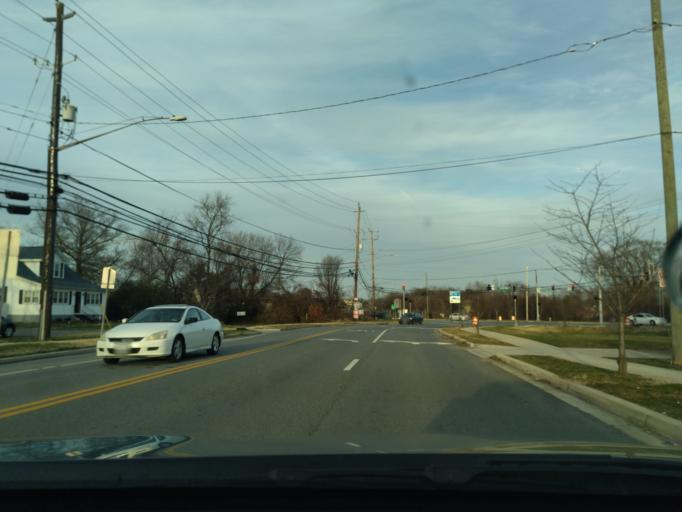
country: US
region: Maryland
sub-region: Prince George's County
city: Clinton
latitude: 38.7513
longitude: -76.8965
